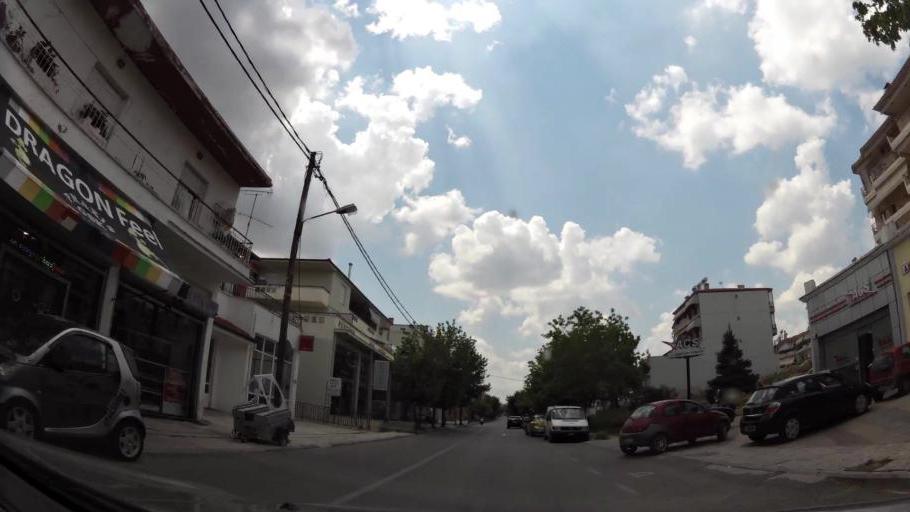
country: GR
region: West Macedonia
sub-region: Nomos Kozanis
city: Kozani
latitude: 40.3027
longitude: 21.8016
